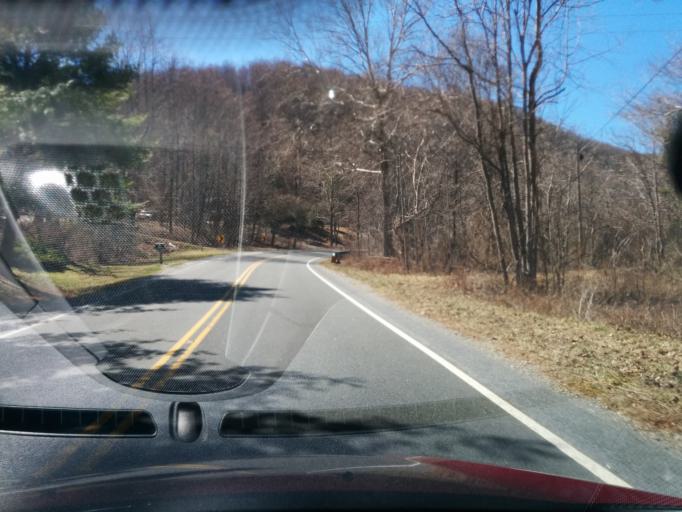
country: US
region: Virginia
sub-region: Nelson County
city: Nellysford
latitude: 37.8787
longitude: -78.9575
